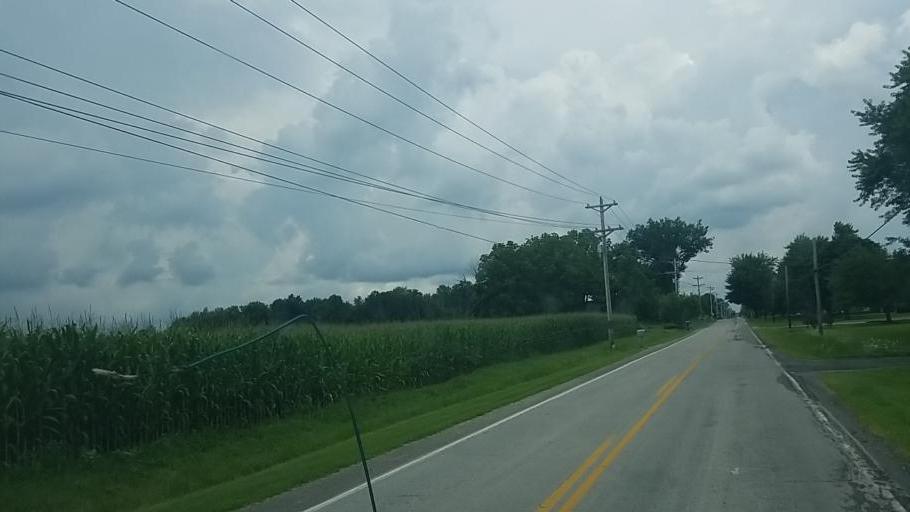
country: US
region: Ohio
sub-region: Lorain County
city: Wellington
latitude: 41.1593
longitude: -82.1694
